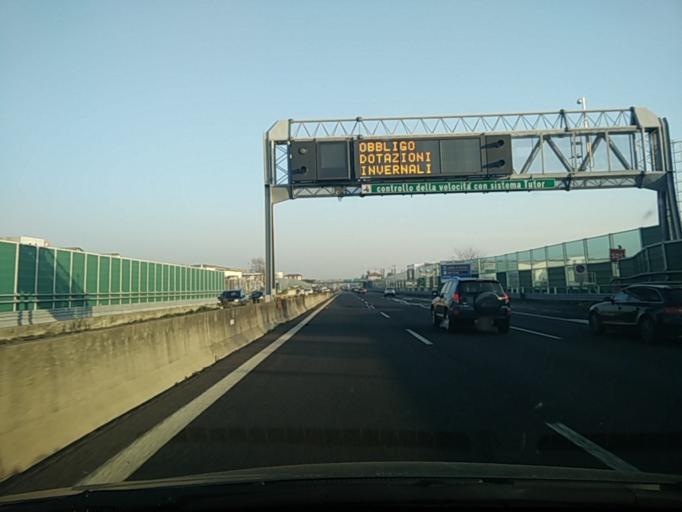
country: IT
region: Lombardy
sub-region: Provincia di Brescia
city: Villa Pedergnano
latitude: 45.5786
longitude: 9.9982
